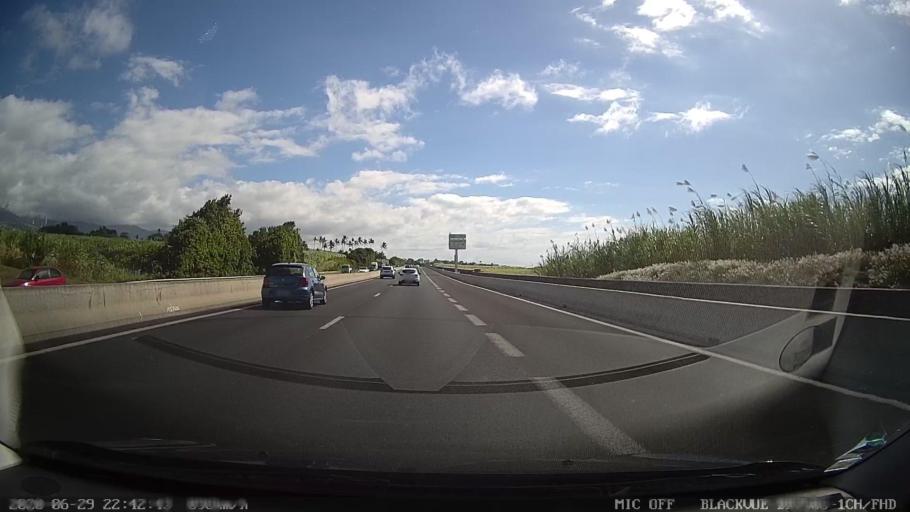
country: RE
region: Reunion
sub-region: Reunion
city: Sainte-Suzanne
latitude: -20.8995
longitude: 55.5854
